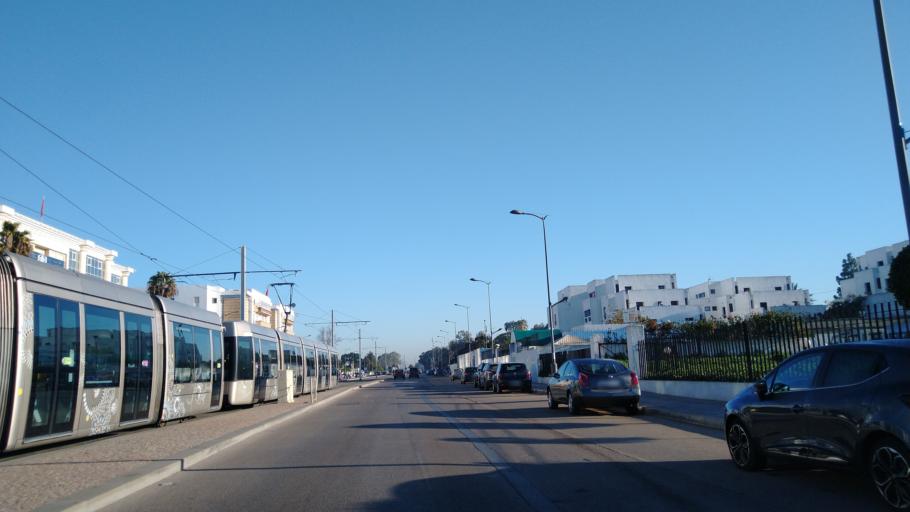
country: MA
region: Rabat-Sale-Zemmour-Zaer
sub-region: Rabat
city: Rabat
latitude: 33.9829
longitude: -6.8639
